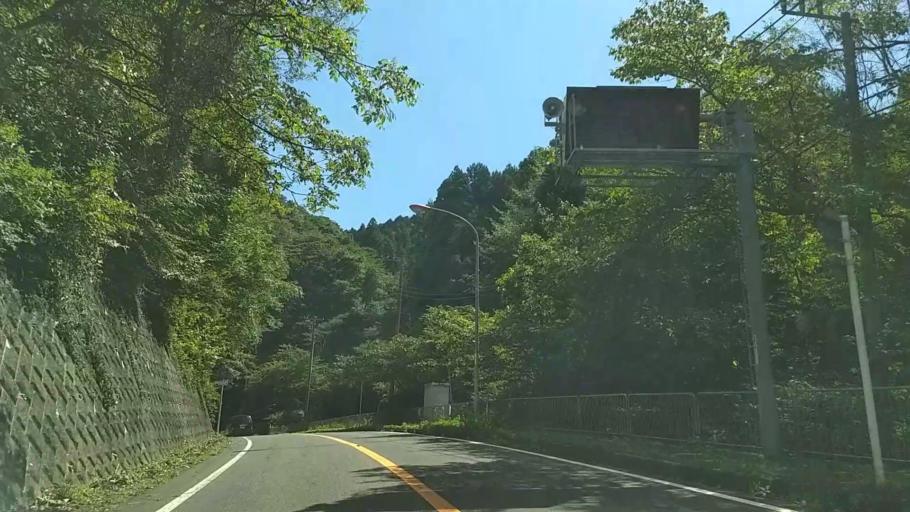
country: JP
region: Tokyo
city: Hachioji
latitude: 35.5569
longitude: 139.2830
